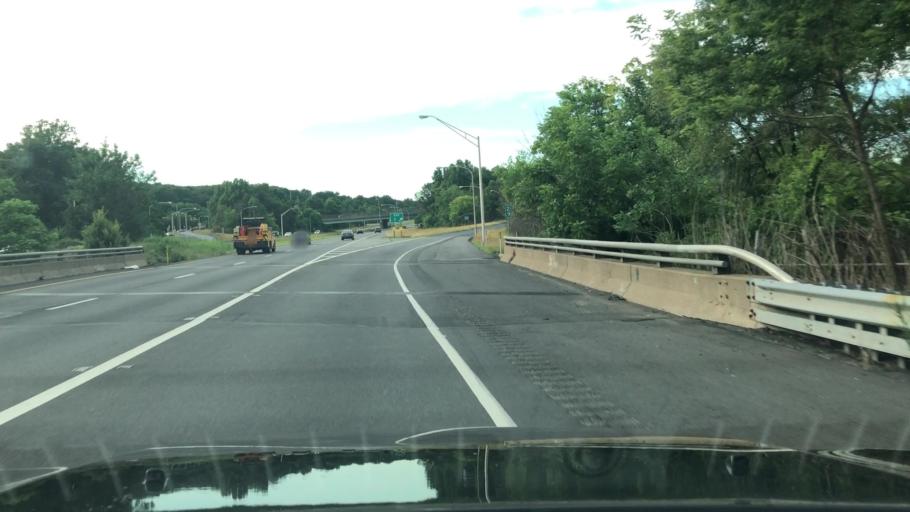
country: US
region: Pennsylvania
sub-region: Bucks County
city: Langhorne Manor
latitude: 40.1616
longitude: -74.9002
